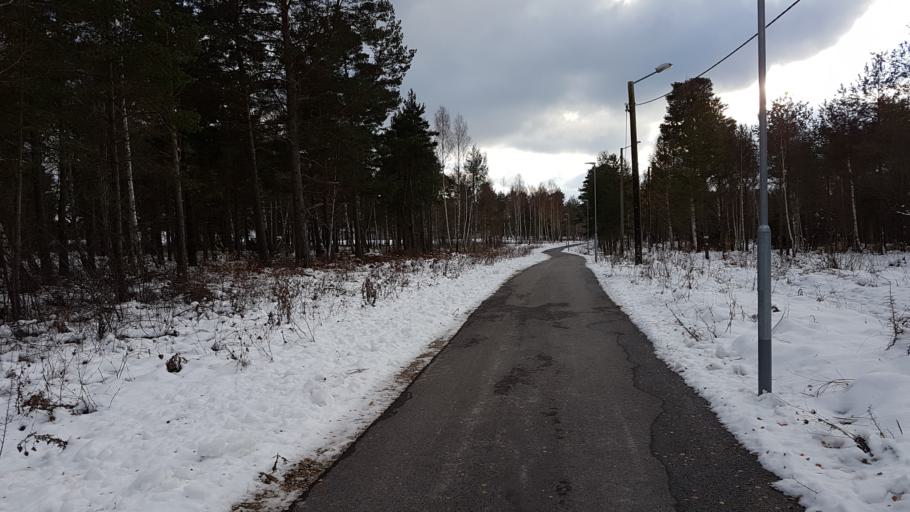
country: SE
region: Gotland
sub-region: Gotland
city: Vibble
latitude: 57.6089
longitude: 18.2805
